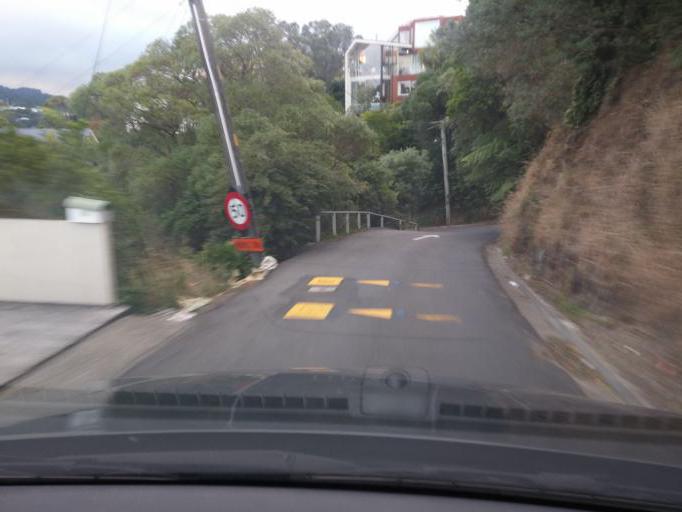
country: NZ
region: Wellington
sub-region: Wellington City
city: Kelburn
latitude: -41.2803
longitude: 174.7628
